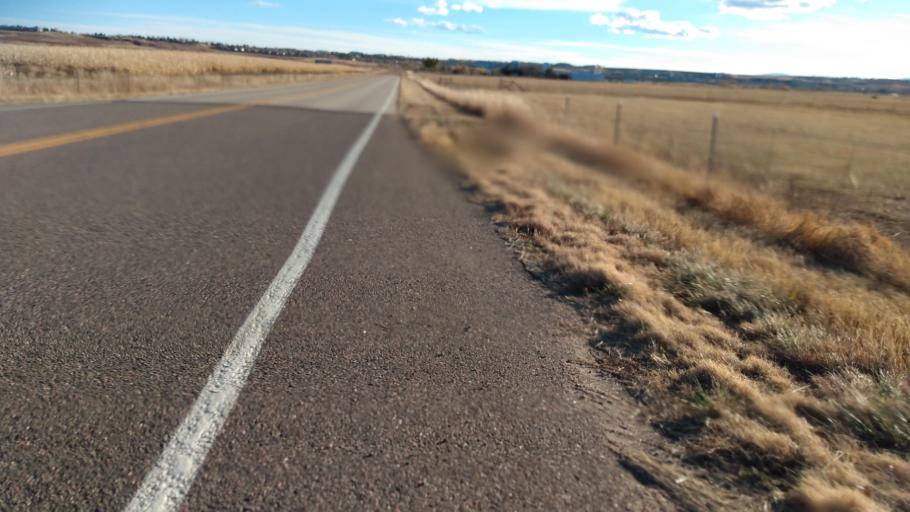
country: US
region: Colorado
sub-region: Boulder County
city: Louisville
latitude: 39.9553
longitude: -105.1104
